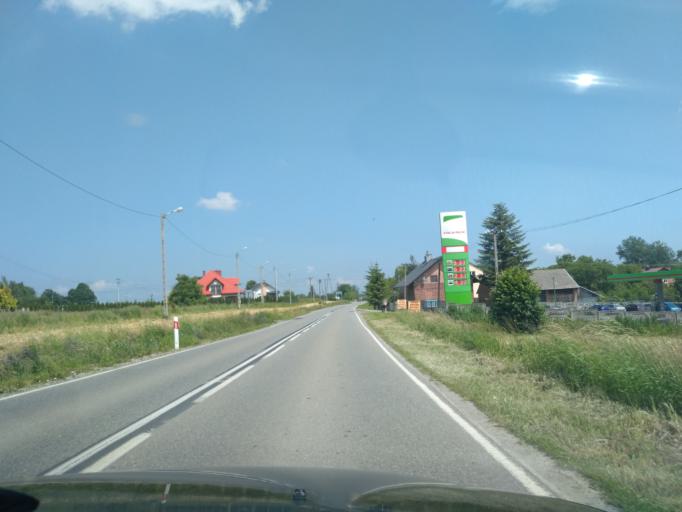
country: PL
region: Subcarpathian Voivodeship
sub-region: Powiat lancucki
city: Albigowa
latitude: 50.0250
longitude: 22.2248
